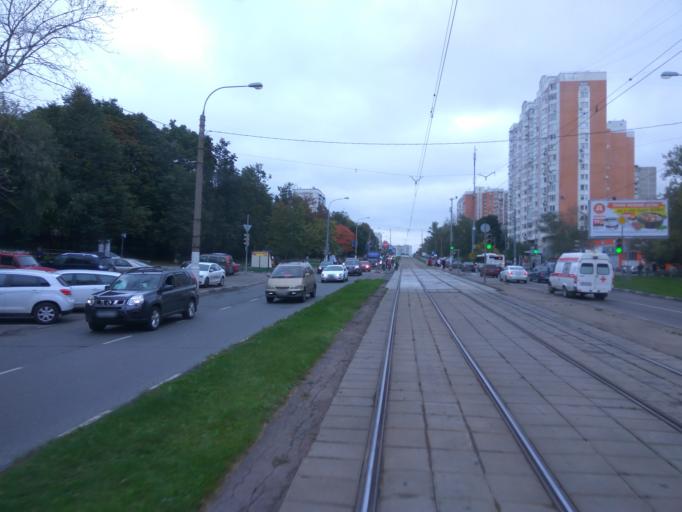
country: RU
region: Moscow
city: Kotlovka
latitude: 55.6484
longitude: 37.6055
